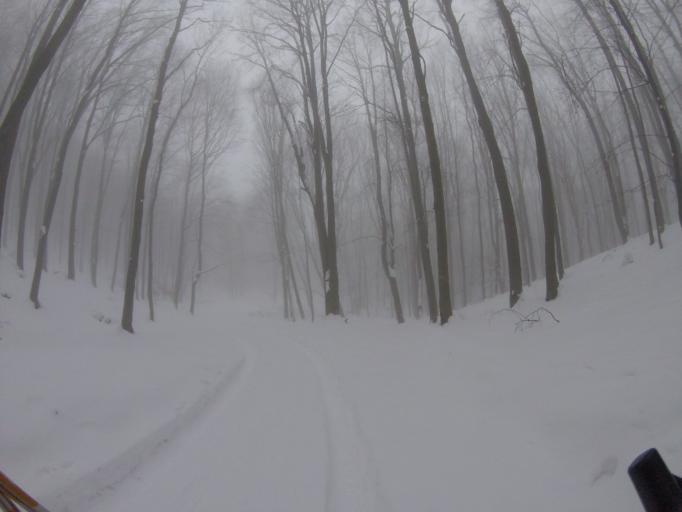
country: HU
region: Heves
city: Szilvasvarad
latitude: 48.0647
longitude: 20.4190
